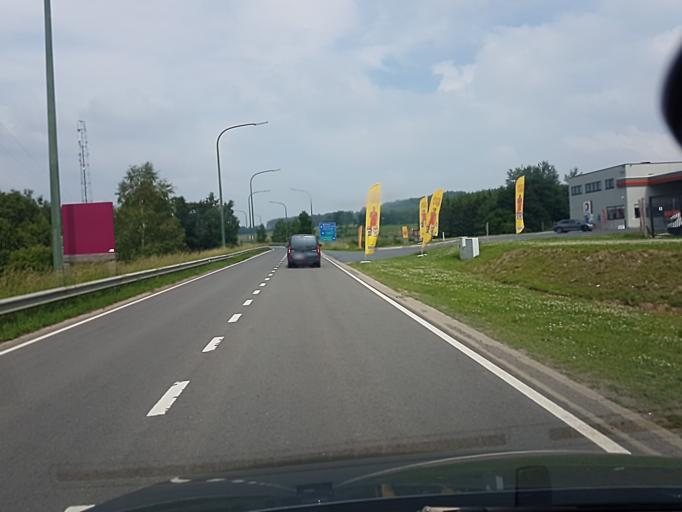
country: BE
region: Wallonia
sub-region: Province du Luxembourg
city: Manhay
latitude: 50.3064
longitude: 5.7116
